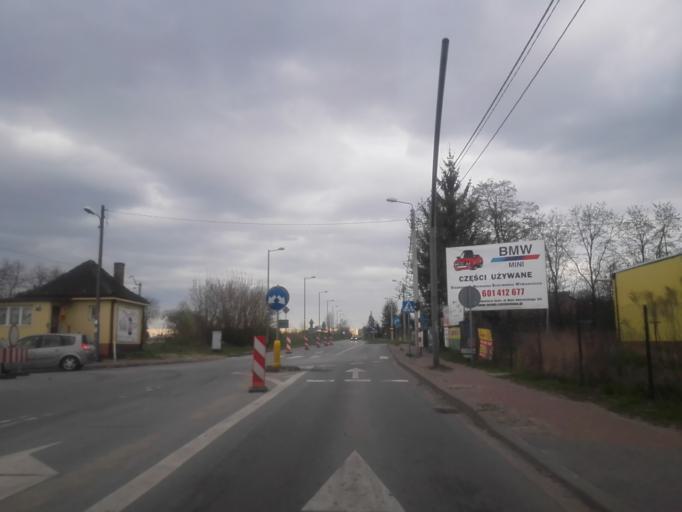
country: PL
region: Silesian Voivodeship
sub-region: Czestochowa
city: Czestochowa
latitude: 50.8295
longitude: 19.1388
